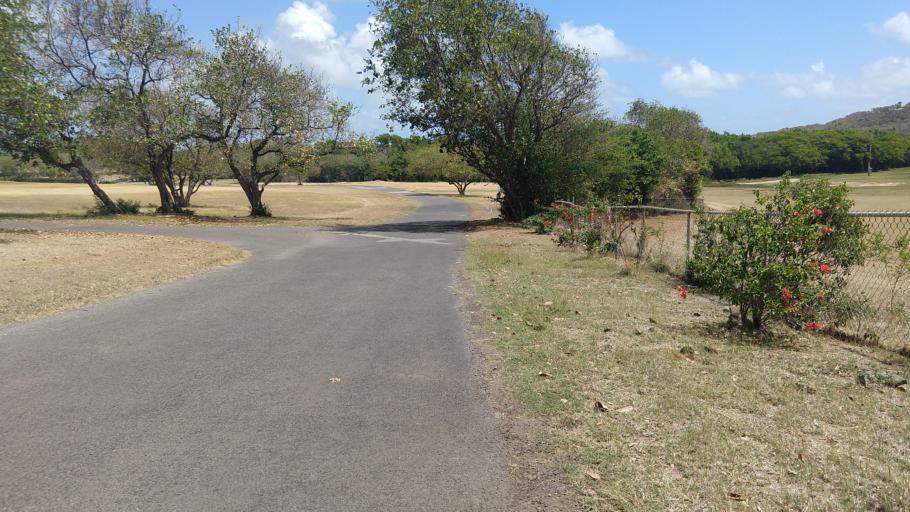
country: VC
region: Grenadines
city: Port Elizabeth
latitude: 12.8865
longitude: -61.1849
